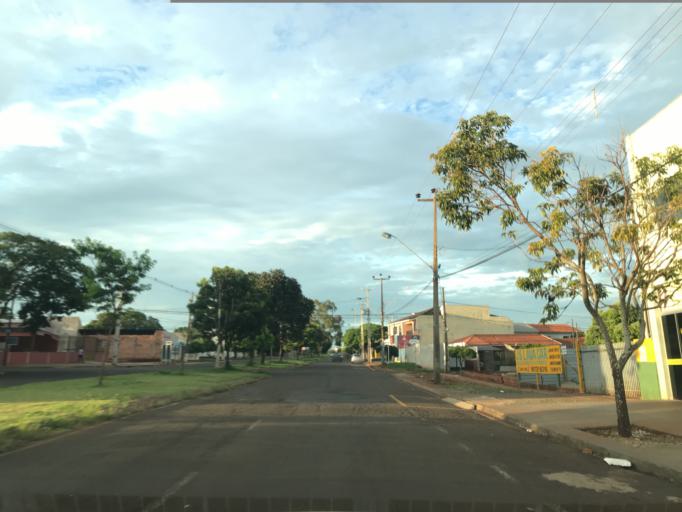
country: BR
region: Parana
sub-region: Maringa
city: Maringa
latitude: -23.3847
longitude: -51.9105
